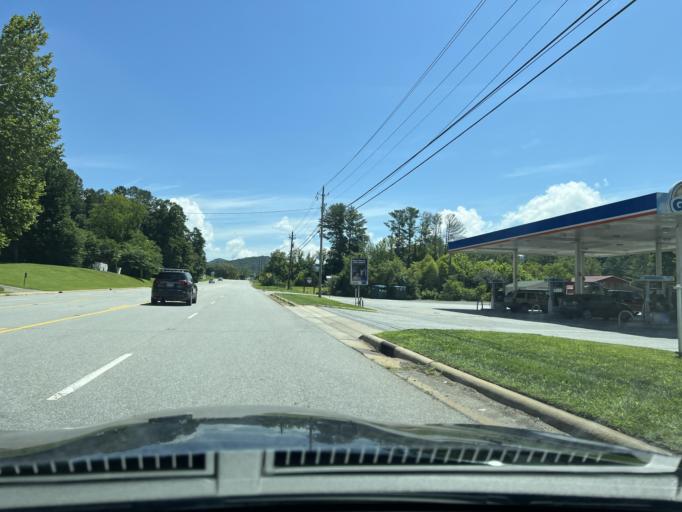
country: US
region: North Carolina
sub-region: Buncombe County
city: Fairview
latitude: 35.5232
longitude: -82.4161
